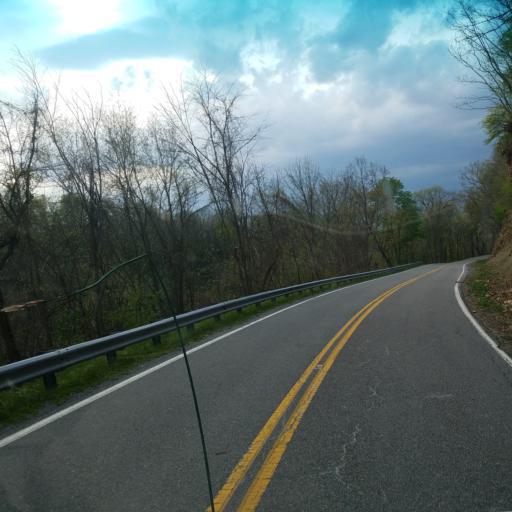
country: US
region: Virginia
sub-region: Smyth County
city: Marion
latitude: 36.9182
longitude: -81.5296
